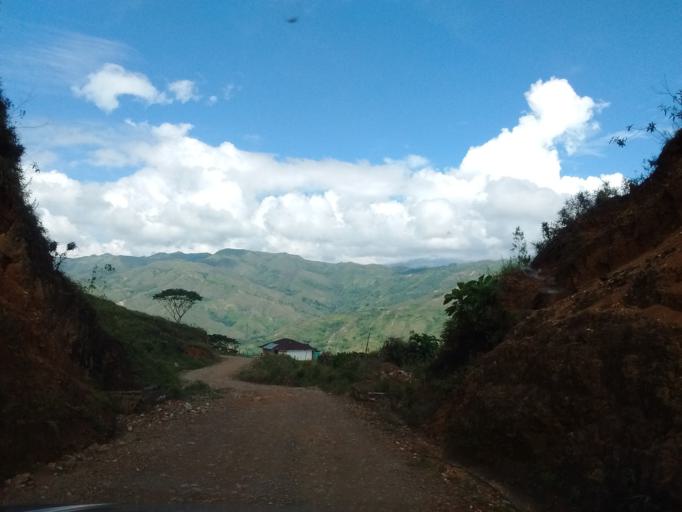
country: CO
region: Cauca
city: Morales
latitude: 2.6929
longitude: -76.7439
